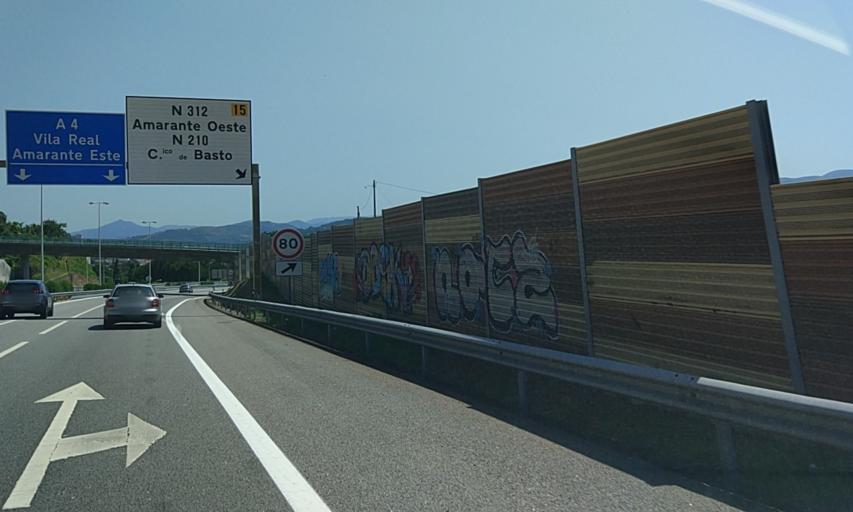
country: PT
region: Porto
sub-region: Amarante
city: Amarante
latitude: 41.2609
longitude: -8.1153
